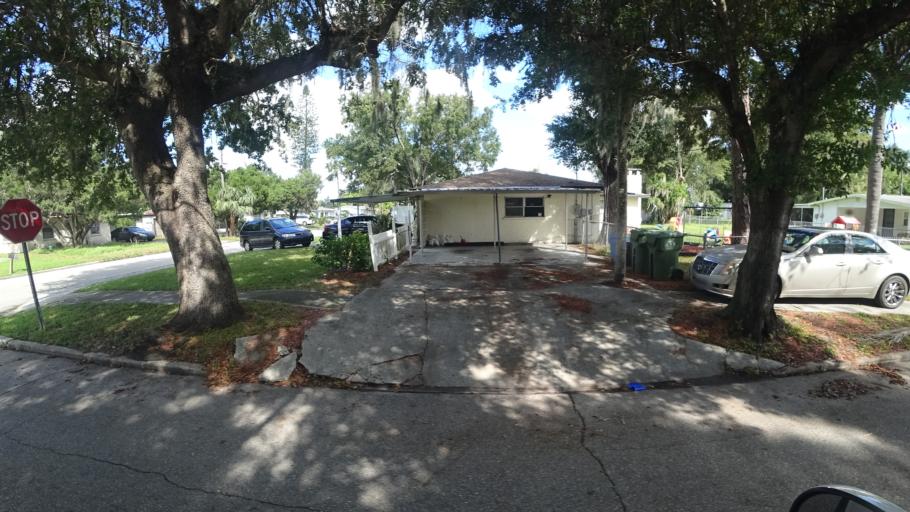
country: US
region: Florida
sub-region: Manatee County
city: Samoset
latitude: 27.4904
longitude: -82.5483
